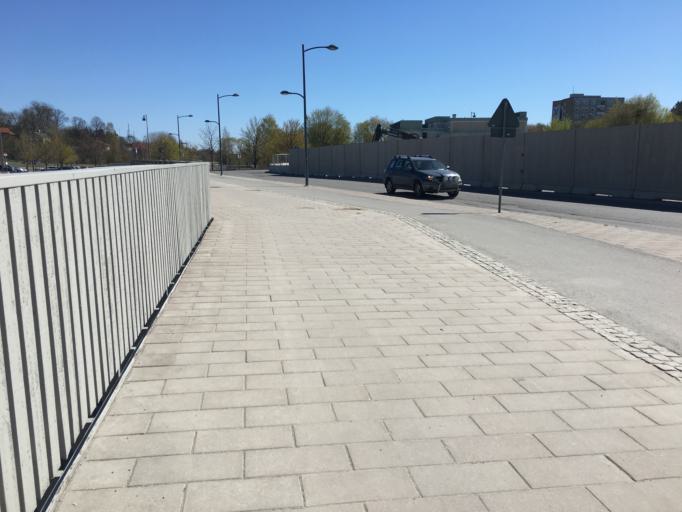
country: SE
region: Stockholm
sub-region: Sundbybergs Kommun
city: Sundbyberg
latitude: 59.3782
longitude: 17.9694
